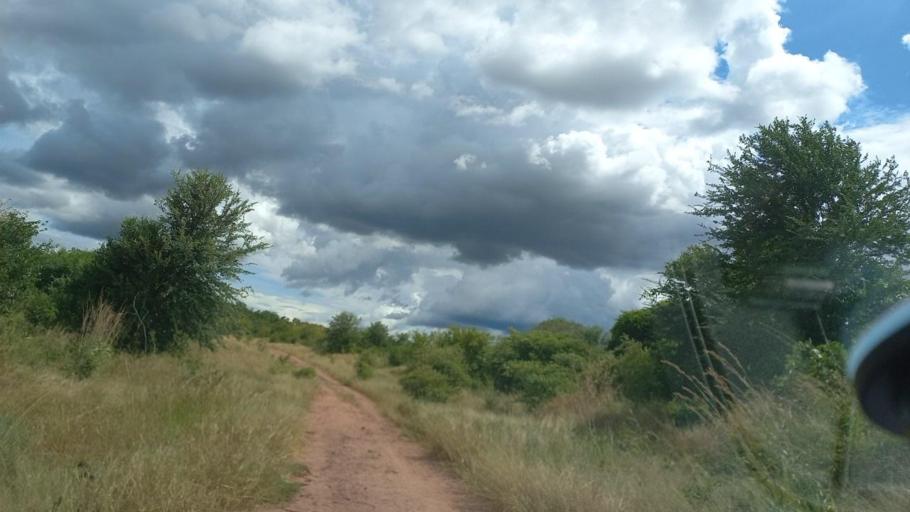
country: ZM
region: Lusaka
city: Luangwa
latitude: -15.6305
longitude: 30.3878
